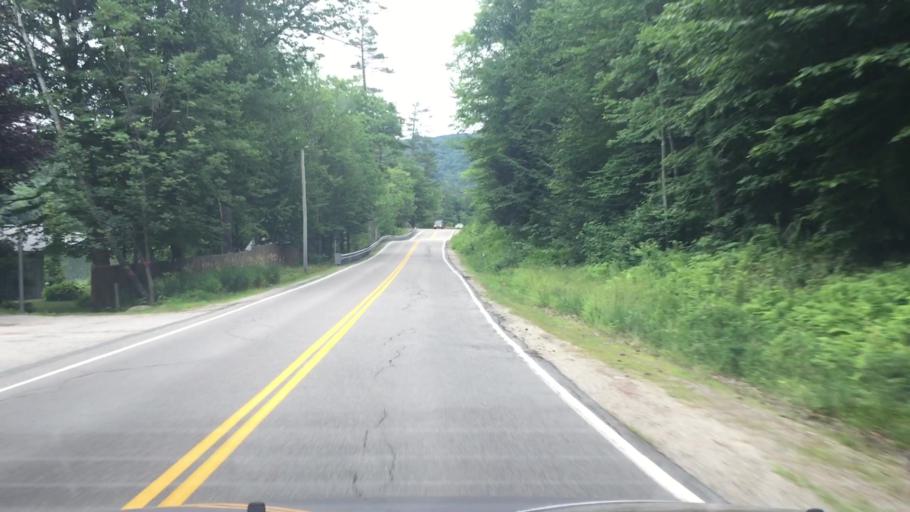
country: US
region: New Hampshire
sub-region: Carroll County
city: Madison
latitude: 43.9078
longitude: -71.0786
